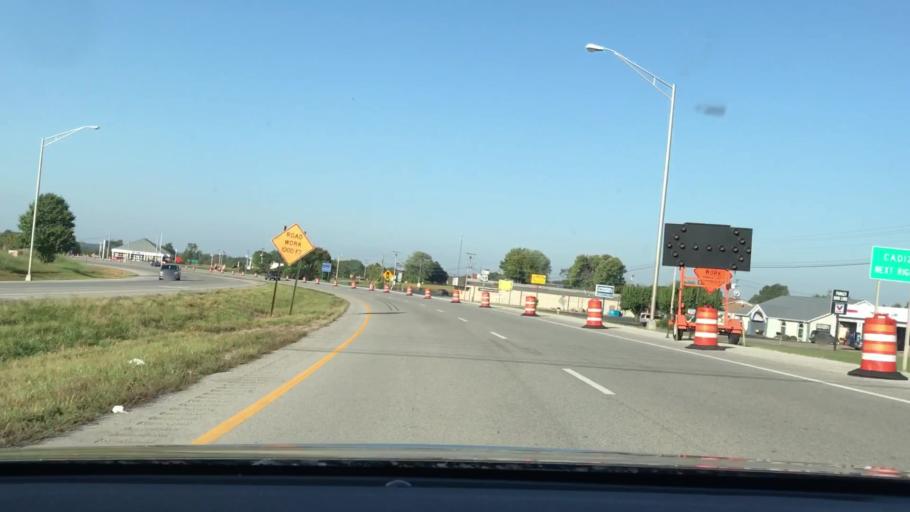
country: US
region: Kentucky
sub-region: Trigg County
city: Cadiz
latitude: 36.8678
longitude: -87.7928
